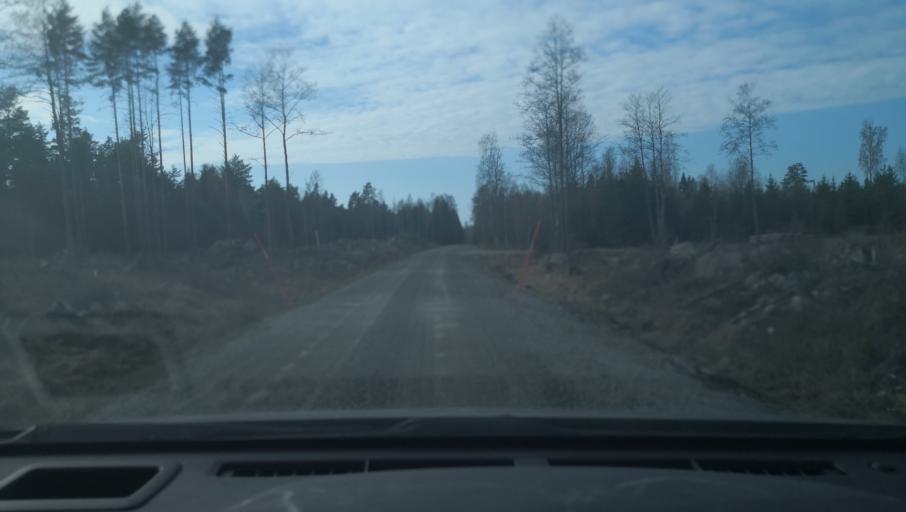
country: SE
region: Uppsala
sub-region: Heby Kommun
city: Heby
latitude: 59.8522
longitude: 16.8742
